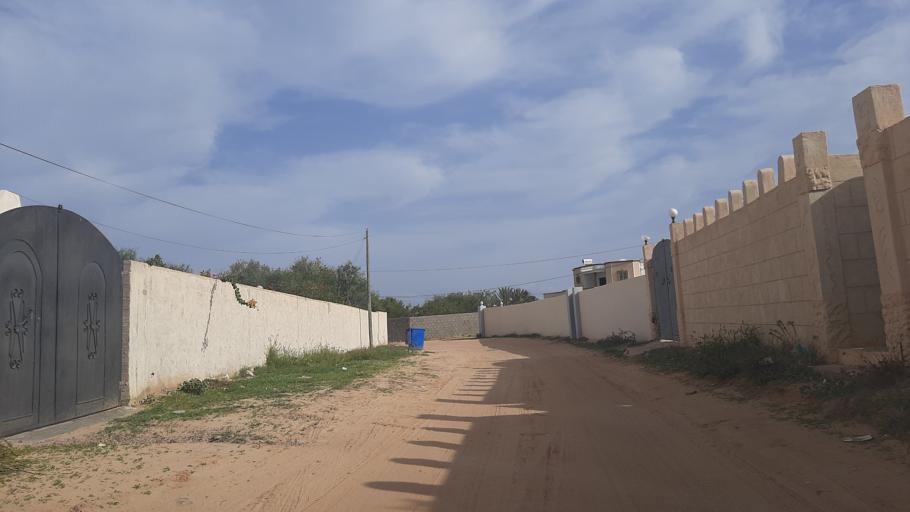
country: TN
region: Madanin
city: Midoun
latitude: 33.8108
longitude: 11.0255
